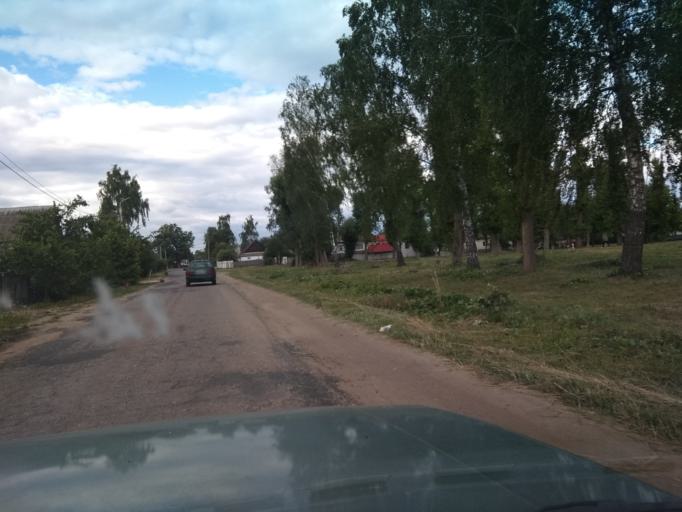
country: BY
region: Mogilev
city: Mahilyow
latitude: 53.9260
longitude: 30.3463
